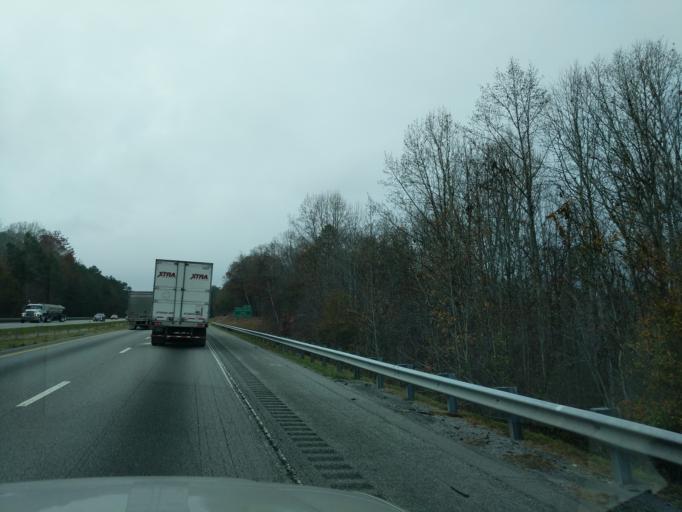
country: US
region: South Carolina
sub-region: Anderson County
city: Centerville
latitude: 34.5507
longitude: -82.7977
